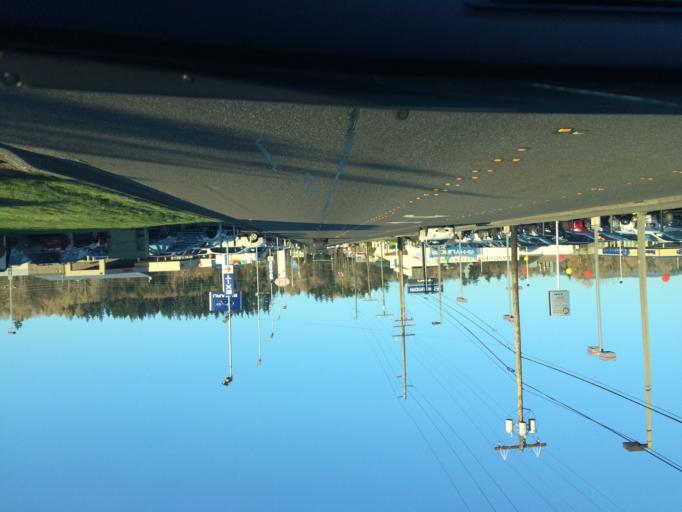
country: US
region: Washington
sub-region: Whatcom County
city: Bellingham
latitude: 48.7564
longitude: -122.4515
